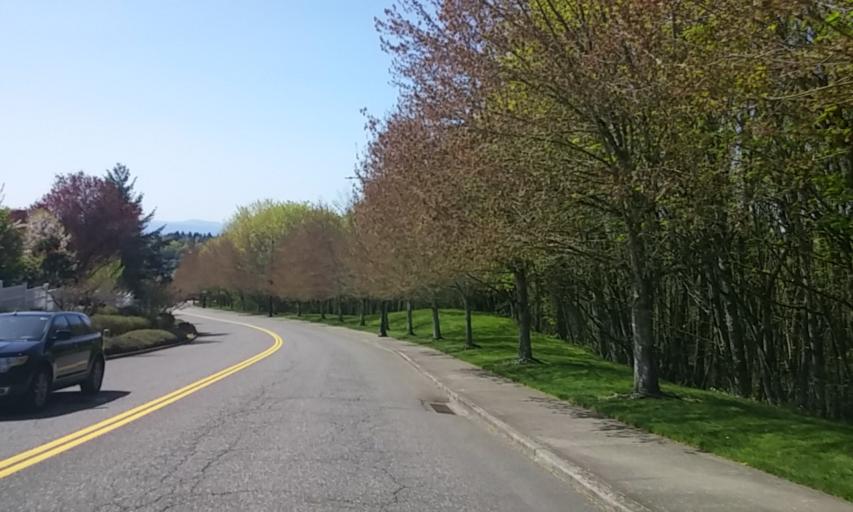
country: US
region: Oregon
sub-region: Washington County
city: West Haven
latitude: 45.5357
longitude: -122.7696
